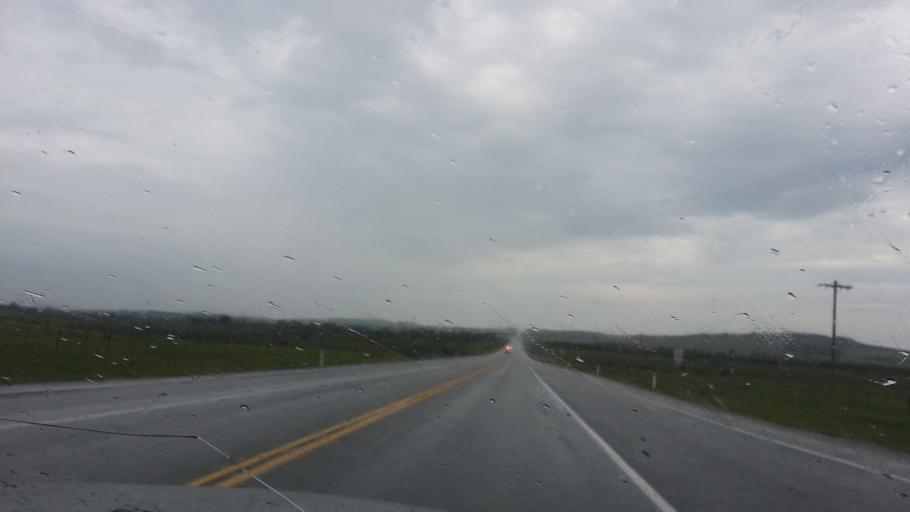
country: CA
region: Alberta
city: Cochrane
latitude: 51.0671
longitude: -114.4668
